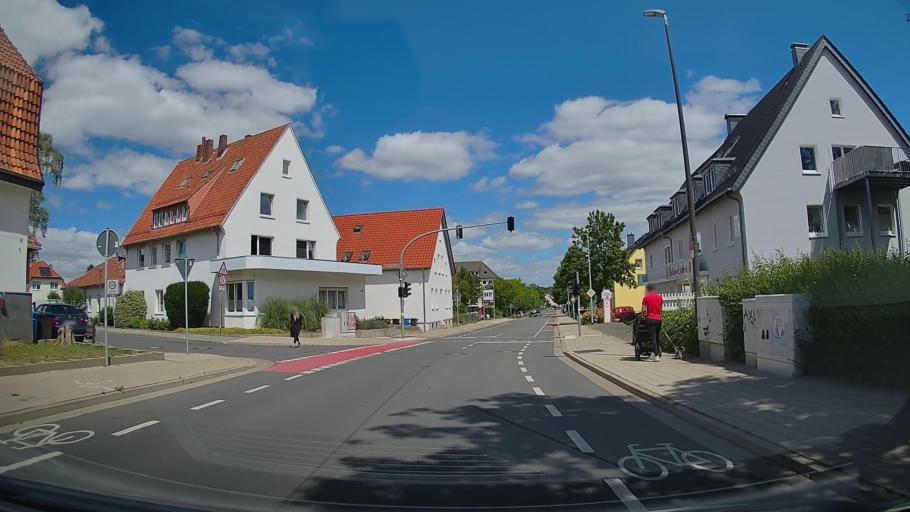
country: DE
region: Lower Saxony
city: Osnabrueck
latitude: 52.2902
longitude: 8.0582
